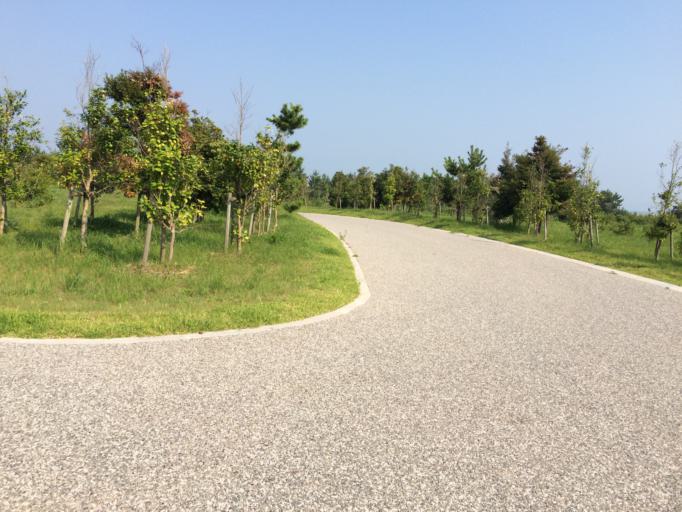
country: JP
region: Yamaguchi
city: Ogori-shimogo
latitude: 34.0095
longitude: 131.3764
